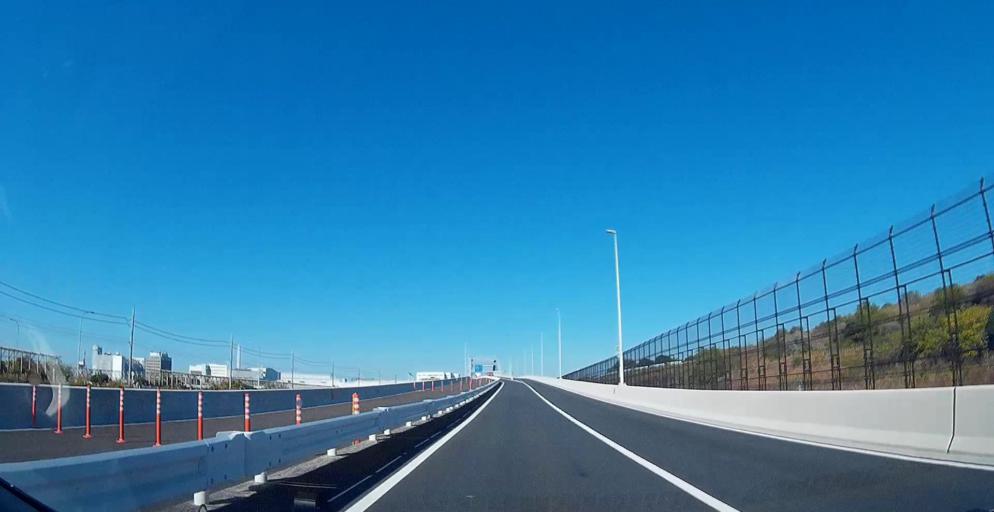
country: JP
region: Tokyo
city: Urayasu
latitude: 35.5963
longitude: 139.8091
